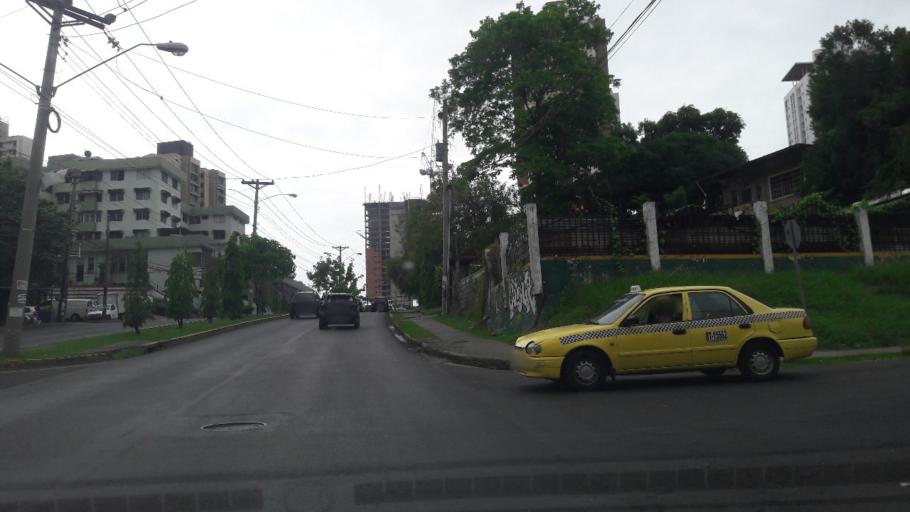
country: PA
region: Panama
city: Panama
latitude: 9.0152
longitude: -79.5140
